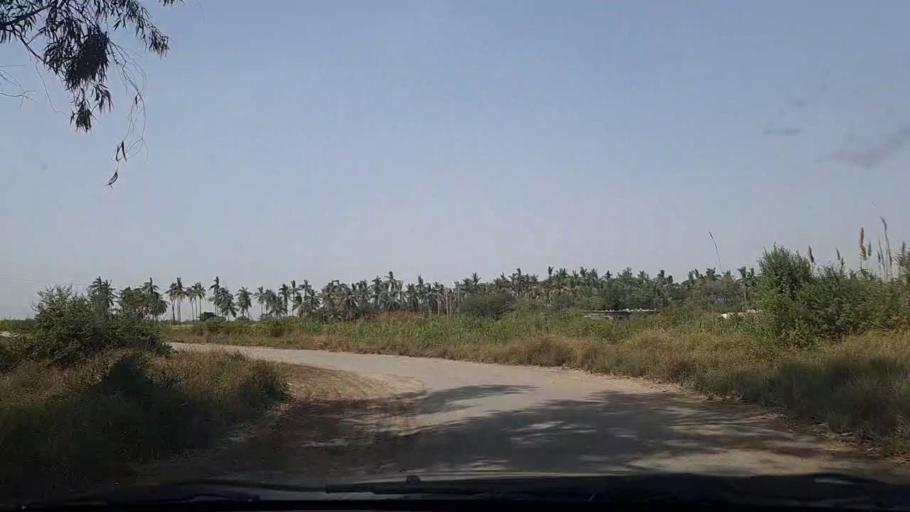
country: PK
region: Sindh
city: Keti Bandar
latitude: 24.2838
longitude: 67.6691
